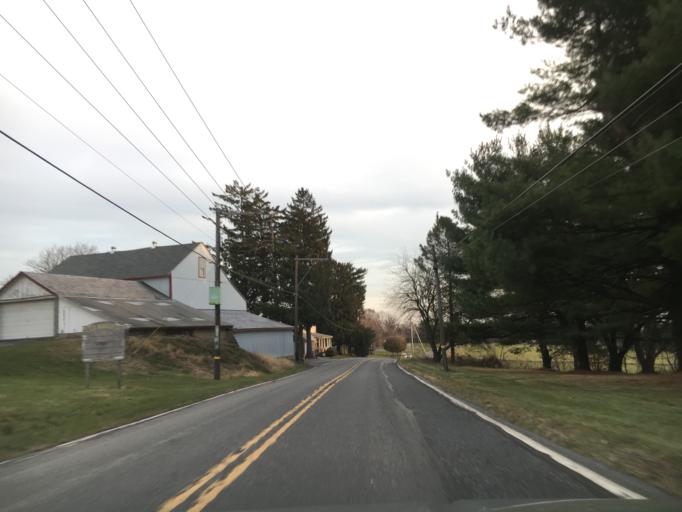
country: US
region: Pennsylvania
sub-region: Lehigh County
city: Slatington
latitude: 40.7177
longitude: -75.6006
